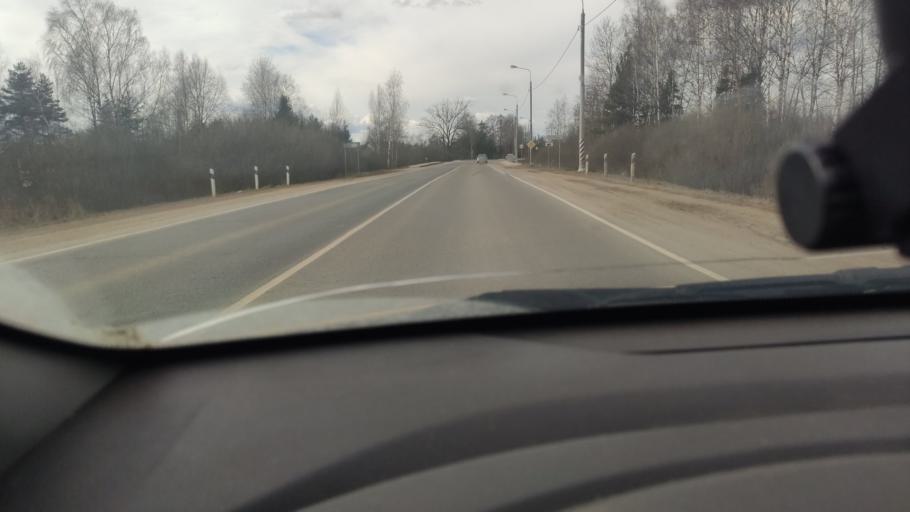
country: RU
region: Moskovskaya
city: Kubinka
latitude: 55.5723
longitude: 36.6661
